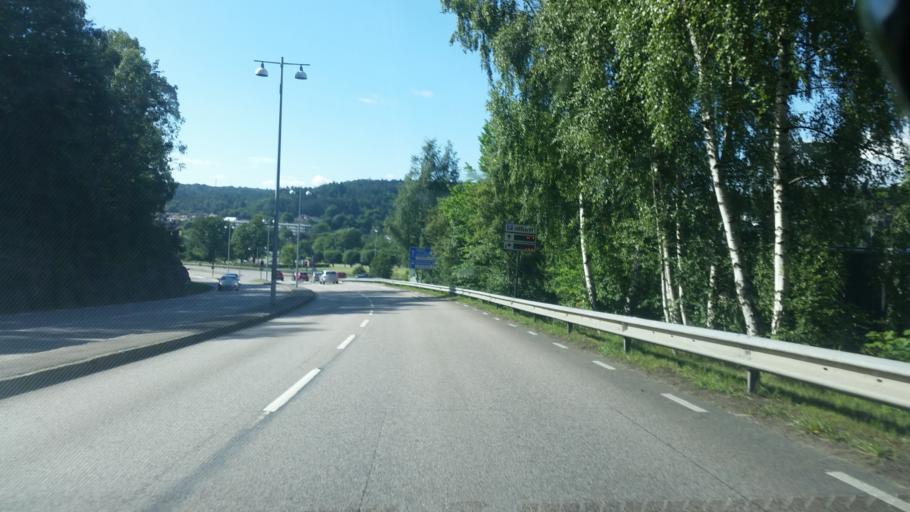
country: SE
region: Vaestra Goetaland
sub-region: Partille Kommun
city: Partille
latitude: 57.7360
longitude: 12.1047
